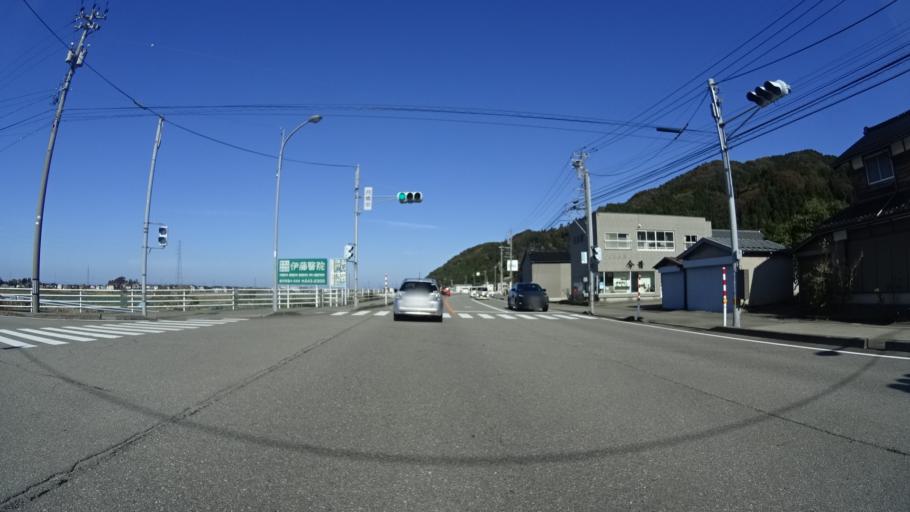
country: JP
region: Ishikawa
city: Tsurugi-asahimachi
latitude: 36.4609
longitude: 136.6210
